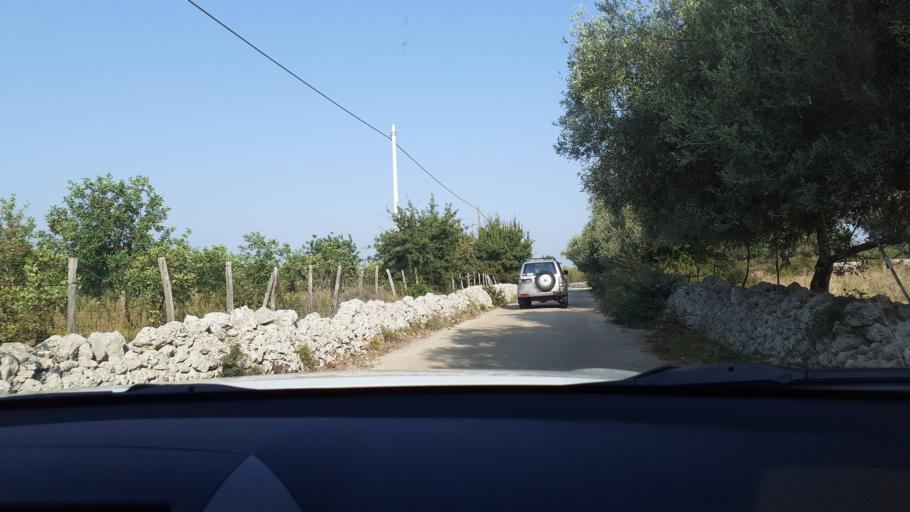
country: IT
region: Sicily
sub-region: Provincia di Siracusa
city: Cassibile
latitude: 36.9788
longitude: 15.1492
